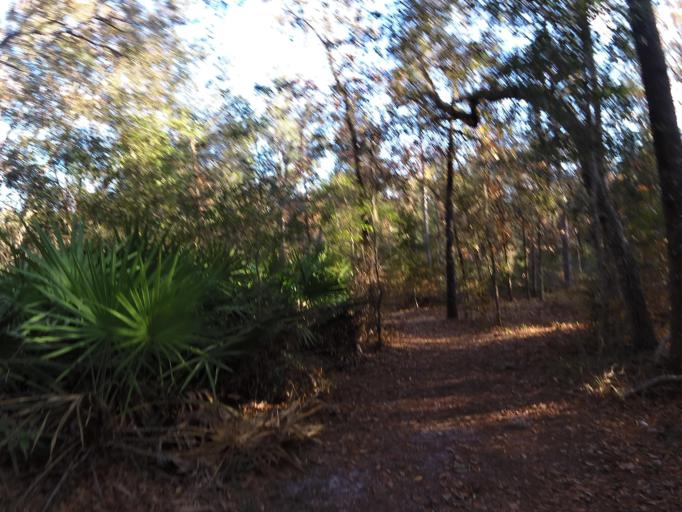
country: US
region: Florida
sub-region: Clay County
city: Middleburg
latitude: 30.1434
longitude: -81.9577
